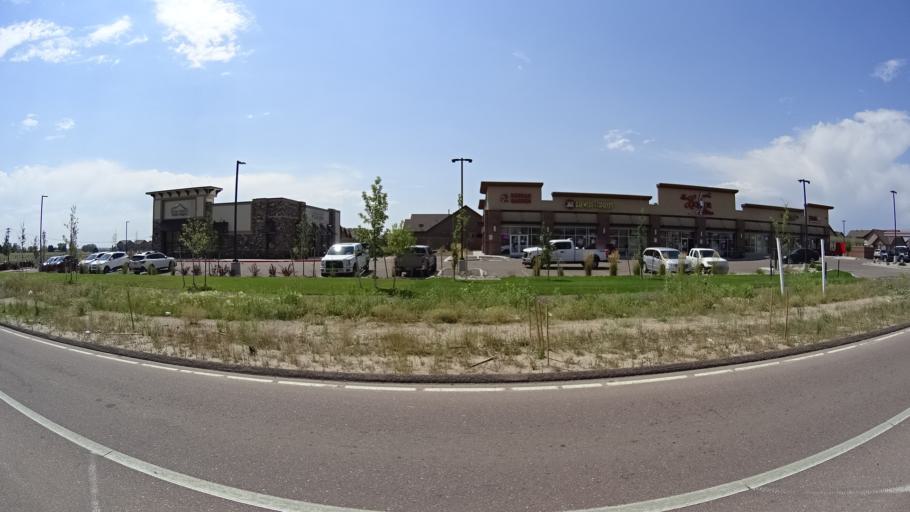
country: US
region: Colorado
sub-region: El Paso County
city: Cimarron Hills
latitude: 38.9264
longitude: -104.6840
